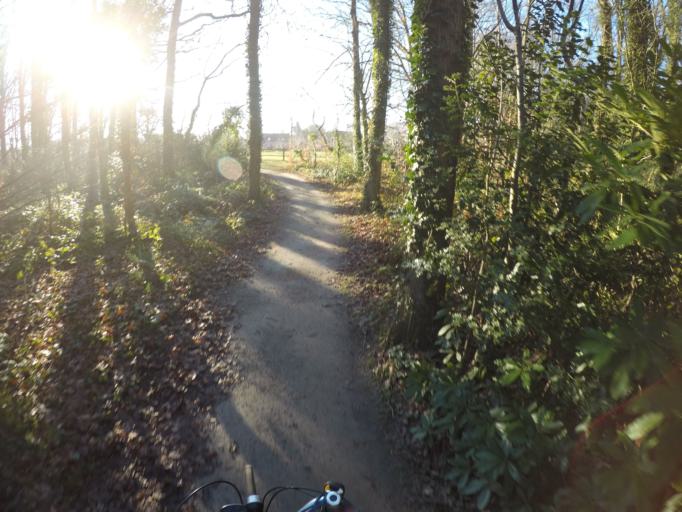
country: BE
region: Flanders
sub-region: Provincie Antwerpen
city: Schilde
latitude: 51.2183
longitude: 4.6102
